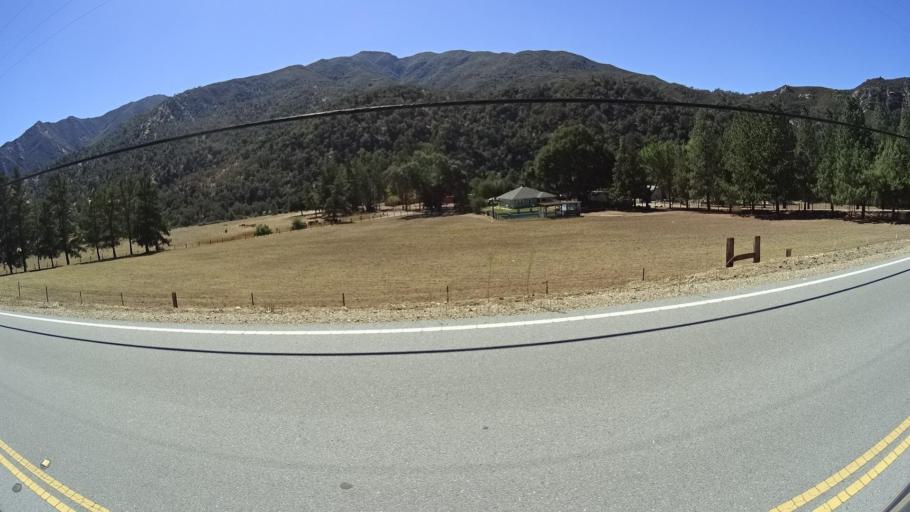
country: US
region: California
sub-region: Monterey County
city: Soledad
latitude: 36.2325
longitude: -121.4646
